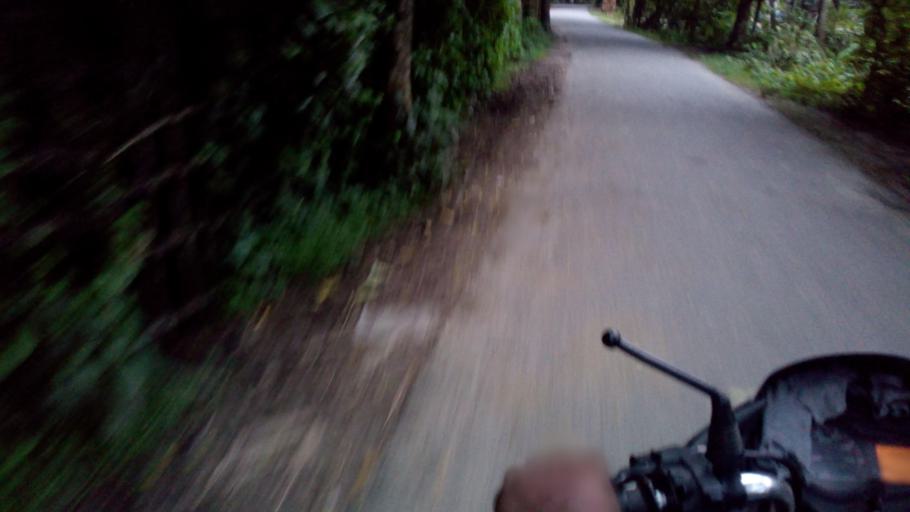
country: BD
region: Khulna
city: Phultala
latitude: 22.7629
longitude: 89.4086
